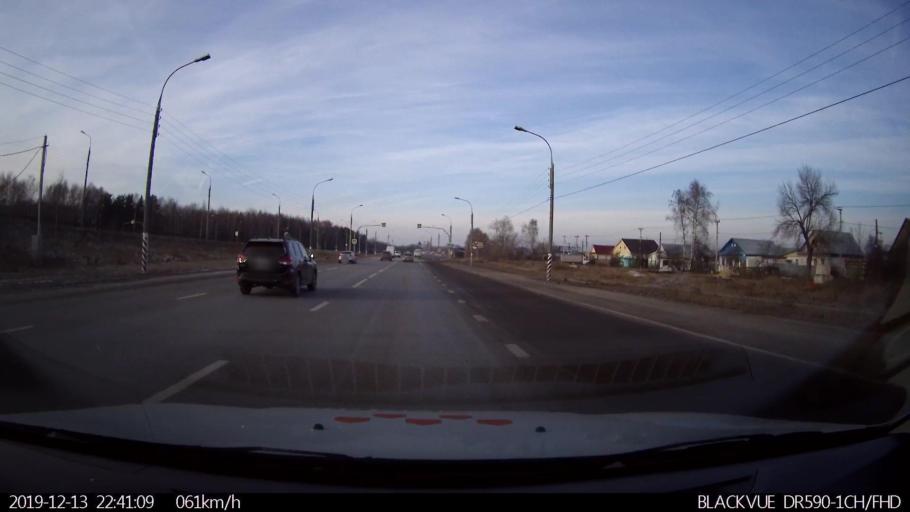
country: RU
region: Nizjnij Novgorod
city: Kstovo
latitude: 56.1816
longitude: 44.1518
